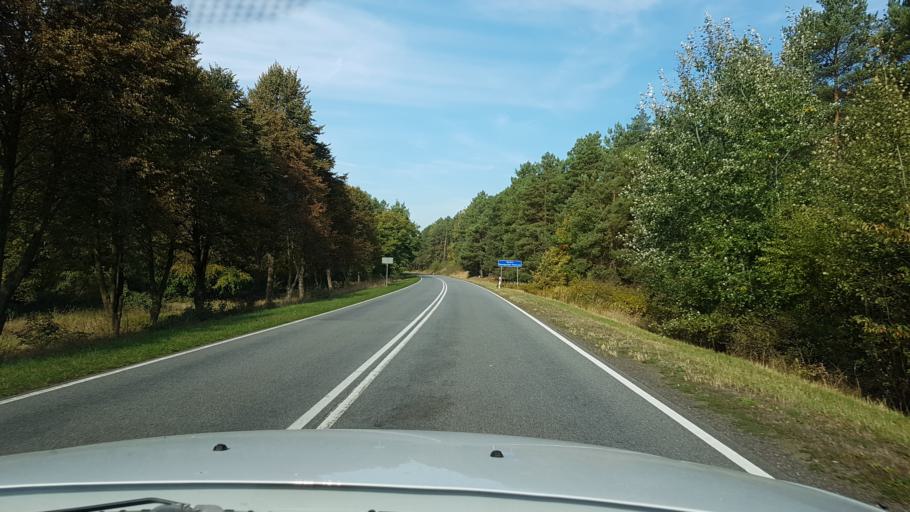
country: PL
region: West Pomeranian Voivodeship
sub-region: Powiat mysliborski
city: Nowogrodek Pomorski
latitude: 52.9171
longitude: 14.9674
